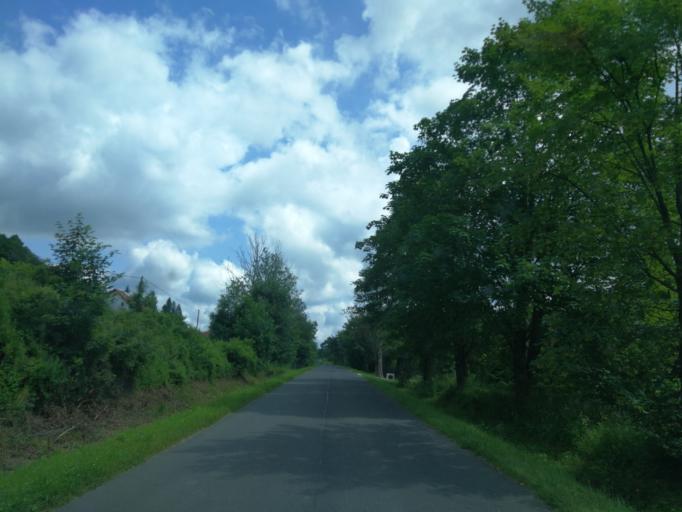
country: PL
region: Subcarpathian Voivodeship
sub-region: Powiat leski
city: Polanczyk
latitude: 49.4204
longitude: 22.4277
